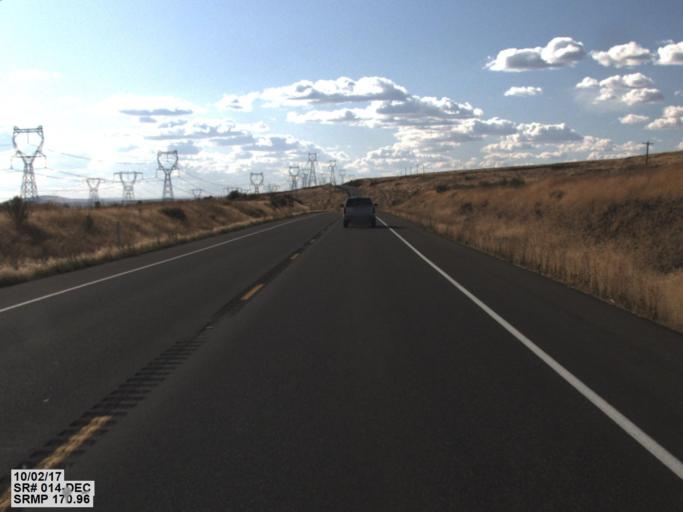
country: US
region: Oregon
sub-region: Morrow County
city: Irrigon
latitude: 45.9438
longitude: -119.5270
